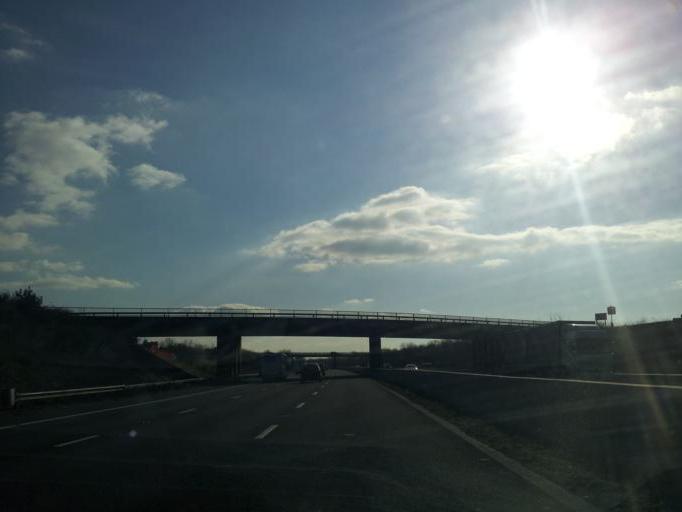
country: GB
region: England
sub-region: North Somerset
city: Kenn
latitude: 51.4336
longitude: -2.8371
